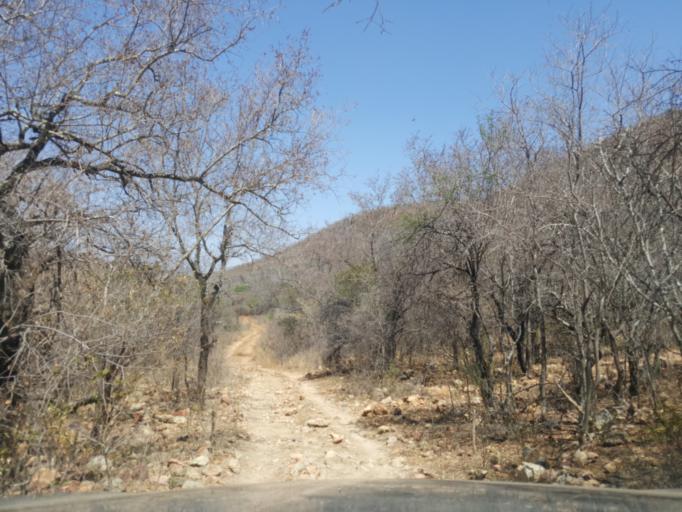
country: BW
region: South East
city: Lobatse
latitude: -25.1563
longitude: 25.6736
